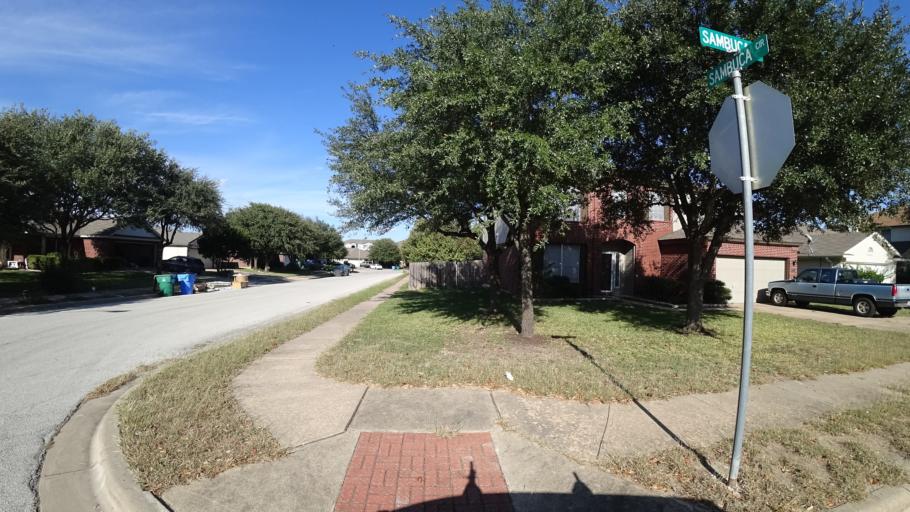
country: US
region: Texas
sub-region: Travis County
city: Wells Branch
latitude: 30.4646
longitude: -97.6865
